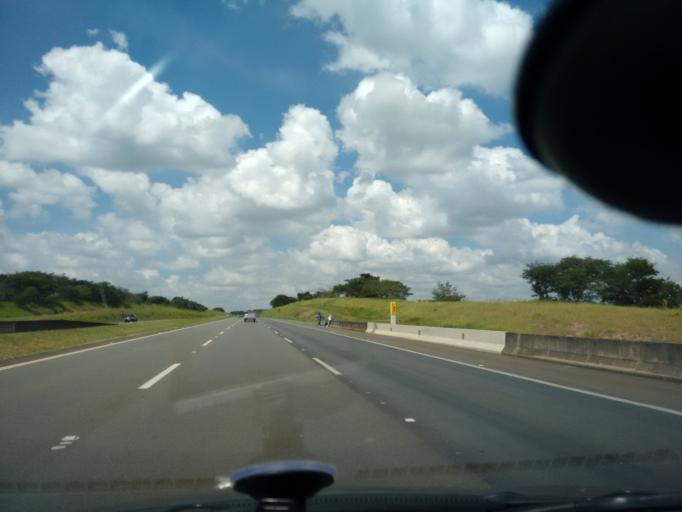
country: BR
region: Sao Paulo
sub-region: Santa Barbara D'Oeste
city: Santa Barbara d'Oeste
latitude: -22.7987
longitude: -47.4056
